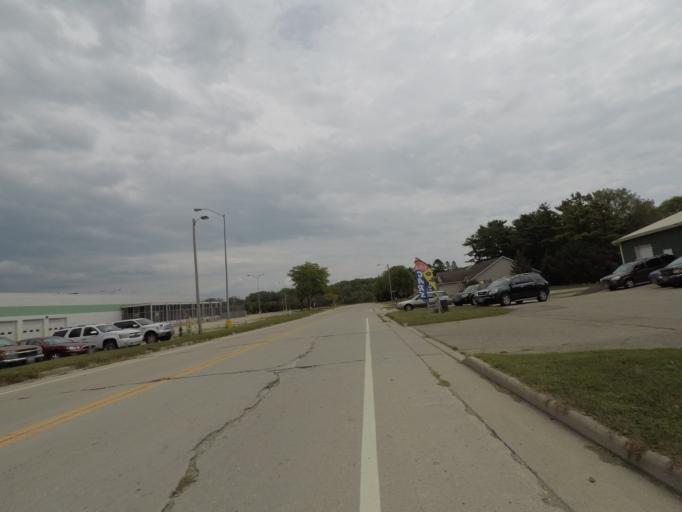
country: US
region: Wisconsin
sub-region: Jefferson County
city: Fort Atkinson
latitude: 42.9421
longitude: -88.8306
